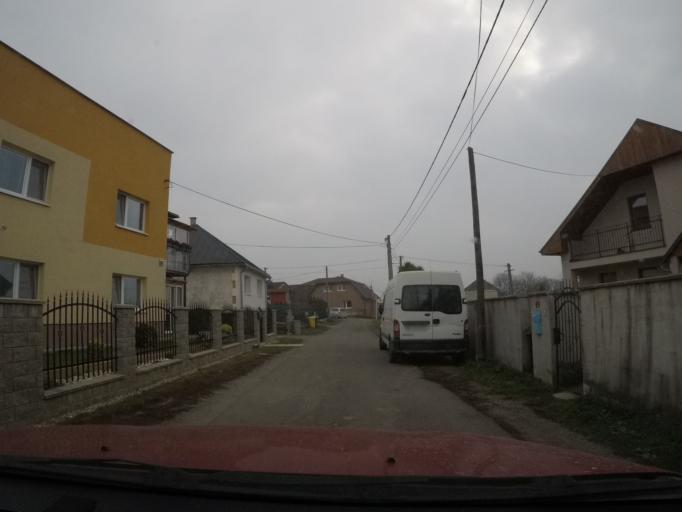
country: SK
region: Presovsky
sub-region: Okres Presov
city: Presov
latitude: 48.8708
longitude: 21.2691
